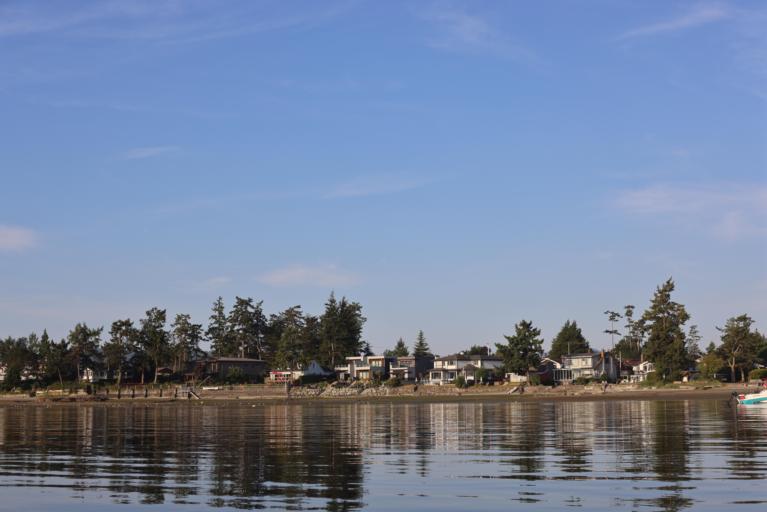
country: CA
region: British Columbia
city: North Saanich
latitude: 48.6640
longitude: -123.4003
